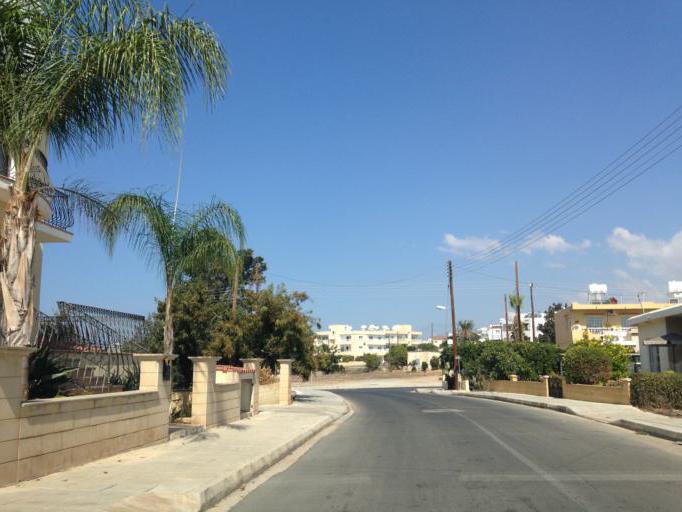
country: CY
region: Pafos
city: Chlorakas
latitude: 34.7987
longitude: 32.4114
